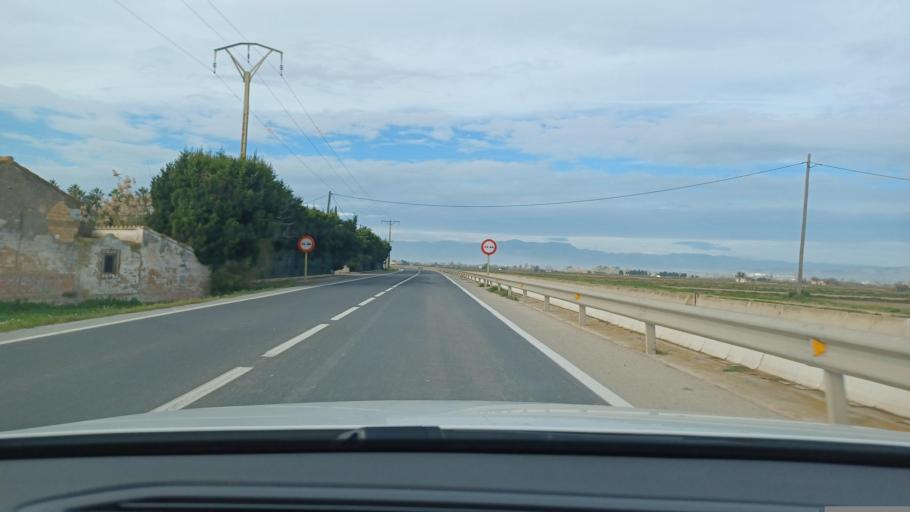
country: ES
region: Catalonia
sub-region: Provincia de Tarragona
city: Deltebre
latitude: 40.7106
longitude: 0.6793
